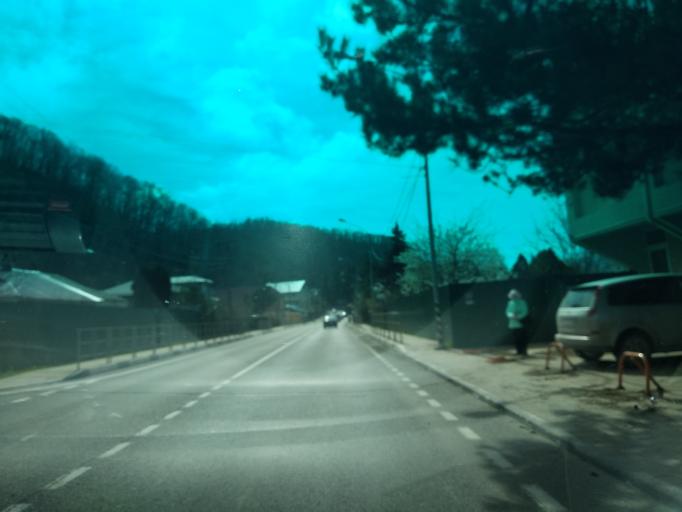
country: RU
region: Krasnodarskiy
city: Shepsi
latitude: 44.0394
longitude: 39.1506
